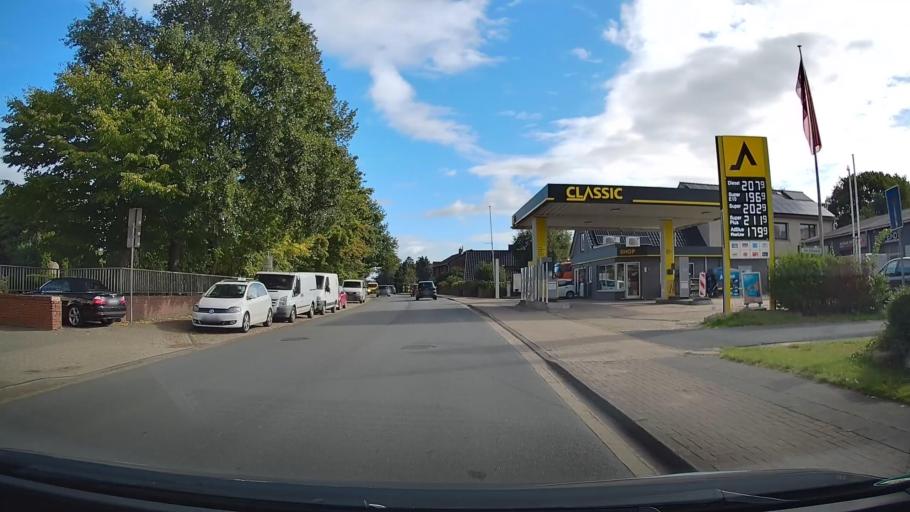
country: DE
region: Lower Saxony
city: Loxstedt
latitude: 53.4468
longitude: 8.5945
